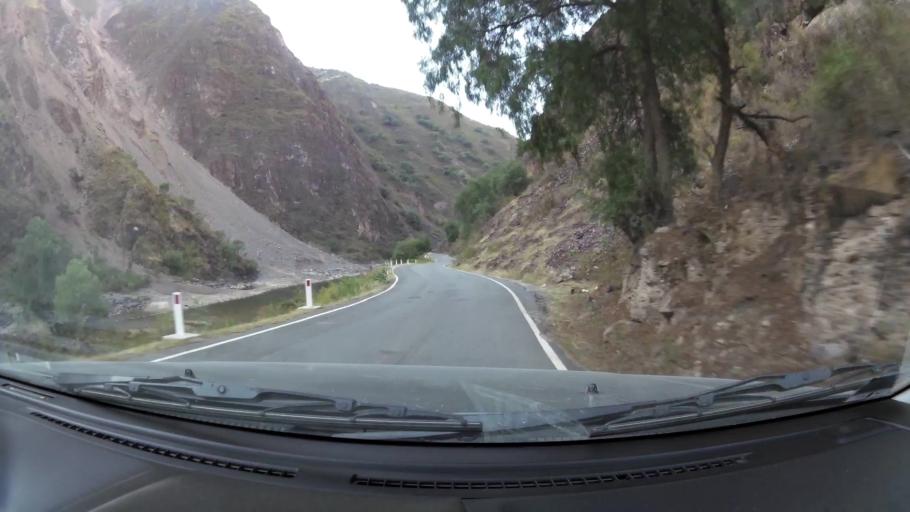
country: PE
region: Huancavelica
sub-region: Provincia de Churcampa
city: La Esmeralda
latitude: -12.5519
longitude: -74.7069
